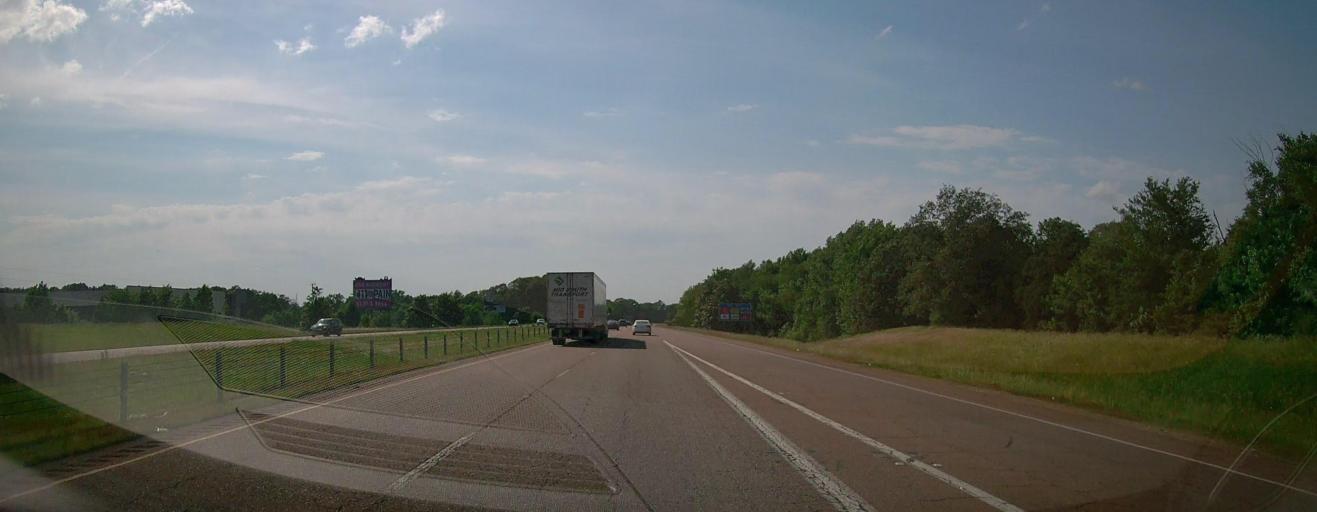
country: US
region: Mississippi
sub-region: De Soto County
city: Olive Branch
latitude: 34.9533
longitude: -89.8427
